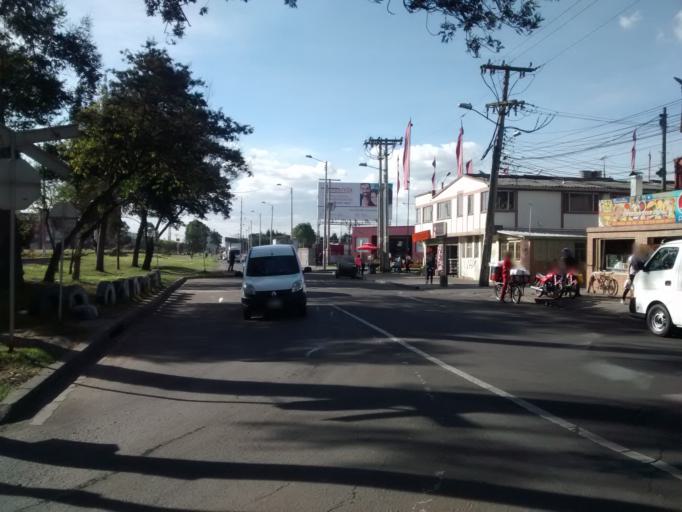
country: CO
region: Bogota D.C.
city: Bogota
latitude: 4.6697
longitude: -74.1339
